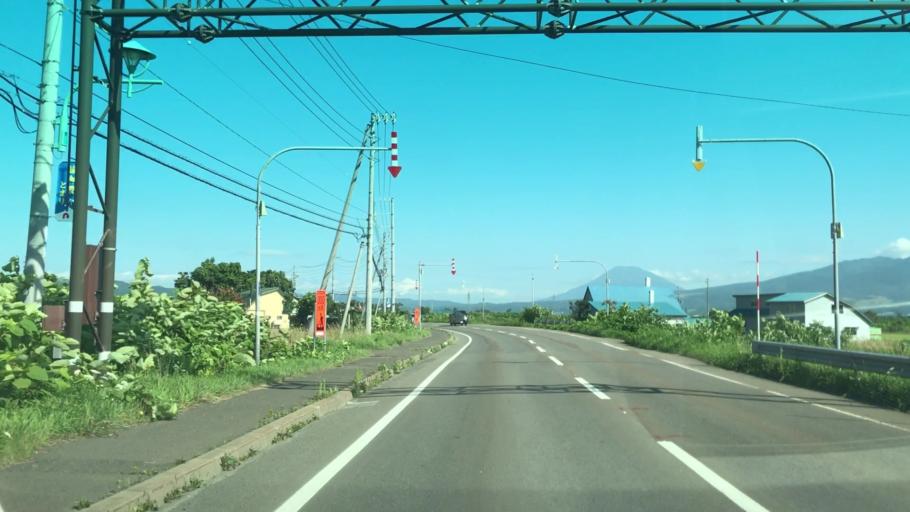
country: JP
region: Hokkaido
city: Iwanai
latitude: 43.0300
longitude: 140.5390
